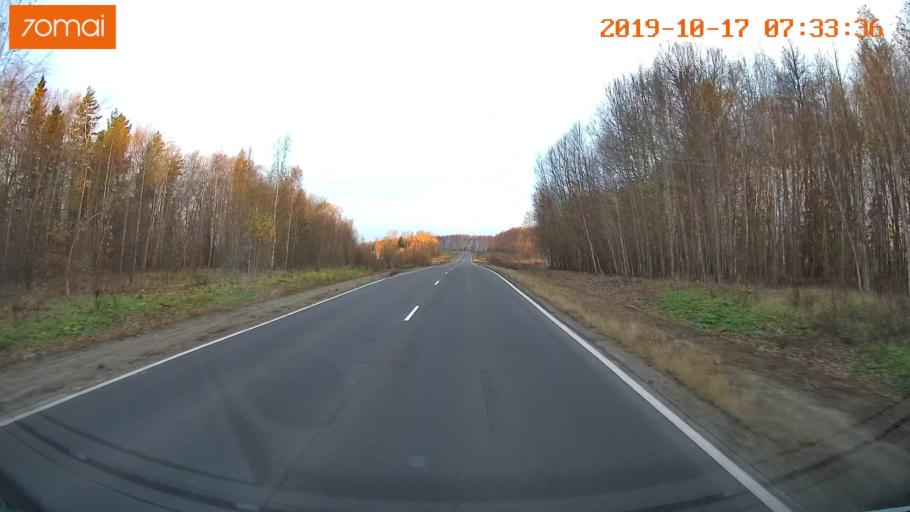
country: RU
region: Ivanovo
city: Gavrilov Posad
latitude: 56.4091
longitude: 39.9555
